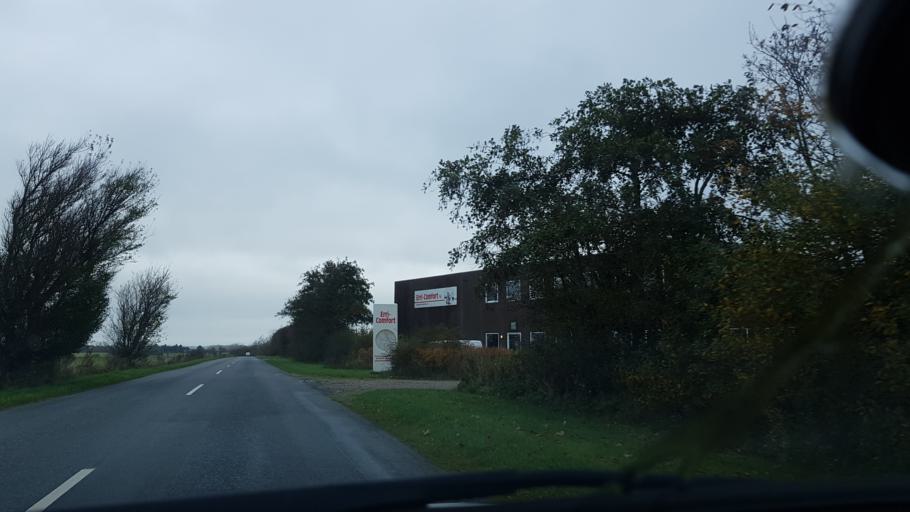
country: DK
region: South Denmark
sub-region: Tonder Kommune
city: Sherrebek
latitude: 55.2225
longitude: 8.8330
